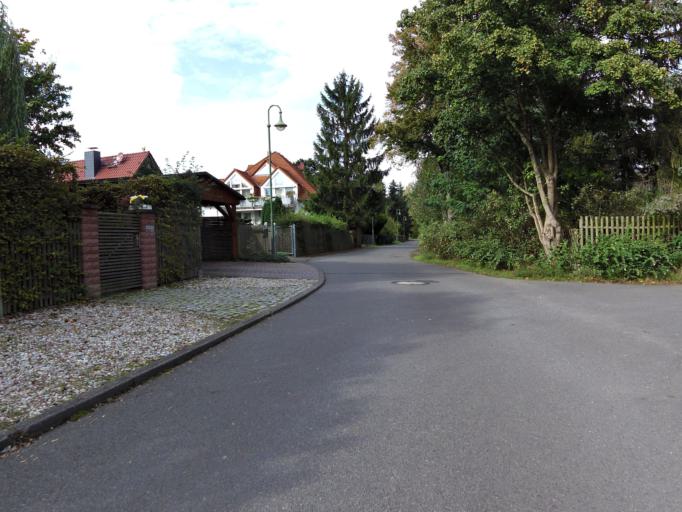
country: DE
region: Saxony
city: Grossposna
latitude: 51.2916
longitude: 12.4500
